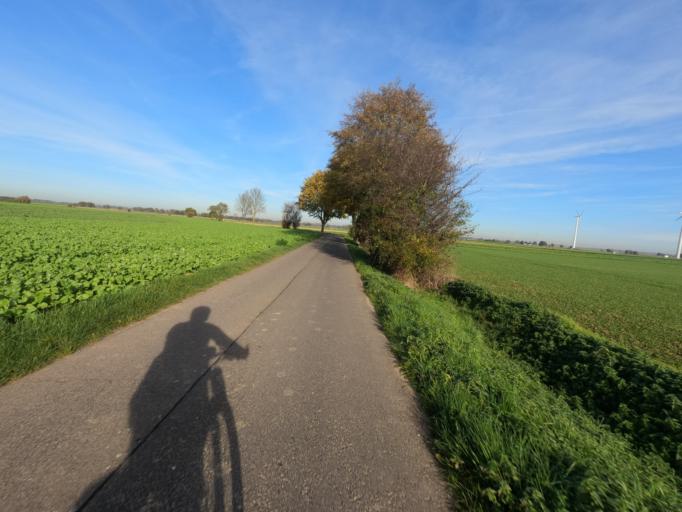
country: DE
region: North Rhine-Westphalia
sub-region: Regierungsbezirk Koln
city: Titz
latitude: 51.0612
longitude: 6.3970
